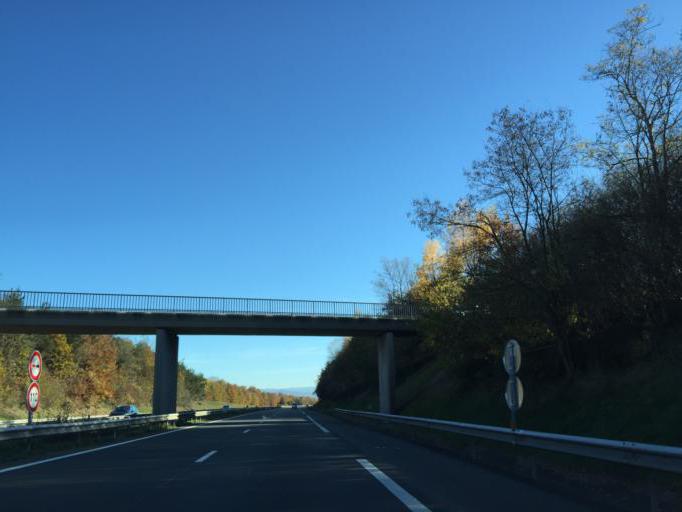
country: FR
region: Rhone-Alpes
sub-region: Departement de la Loire
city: Balbigny
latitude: 45.7754
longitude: 4.1505
